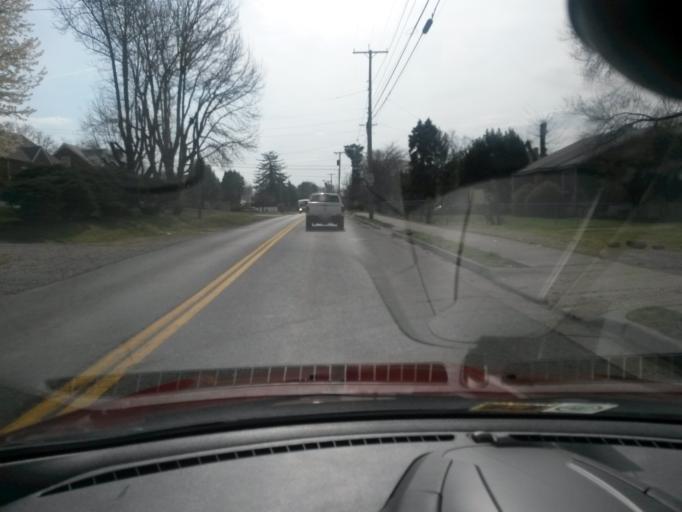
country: US
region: Virginia
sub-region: City of Roanoke
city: Roanoke
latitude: 37.3001
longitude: -79.9756
